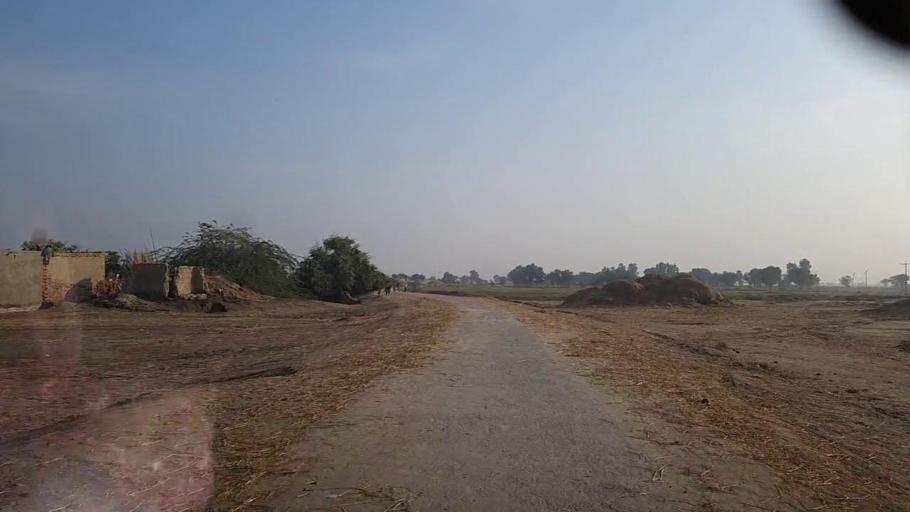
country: PK
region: Sindh
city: Jacobabad
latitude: 28.2355
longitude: 68.4849
